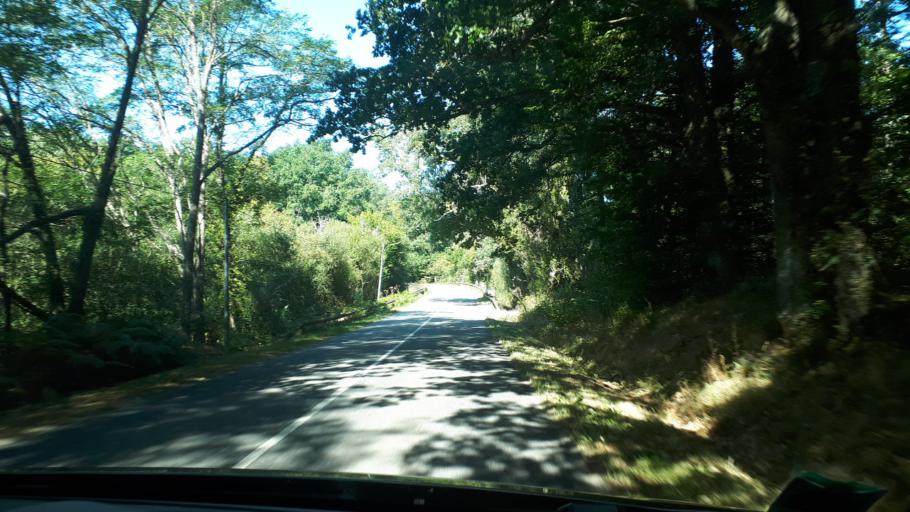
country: FR
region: Centre
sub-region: Departement du Loiret
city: Saint-Brisson-sur-Loire
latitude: 47.5962
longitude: 2.6887
